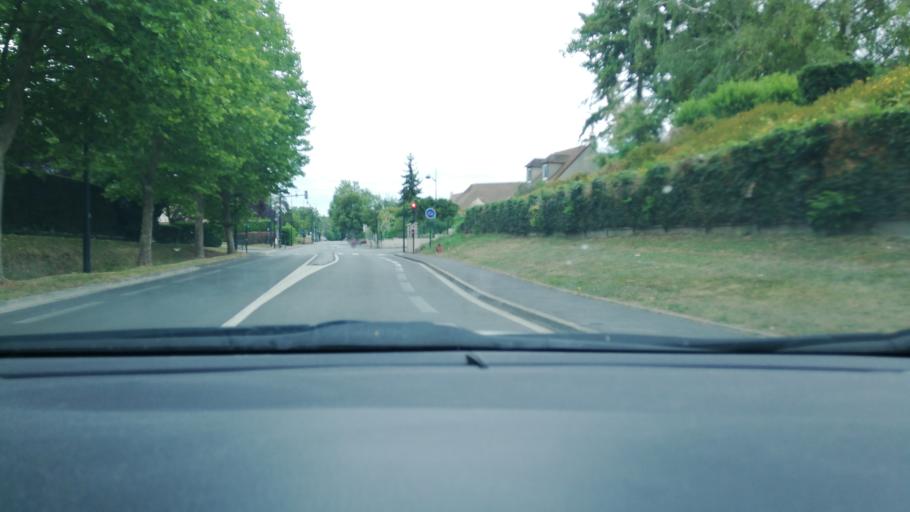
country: FR
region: Ile-de-France
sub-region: Departement du Val-d'Oise
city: Auvers-sur-Oise
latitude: 49.0768
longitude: 2.1607
